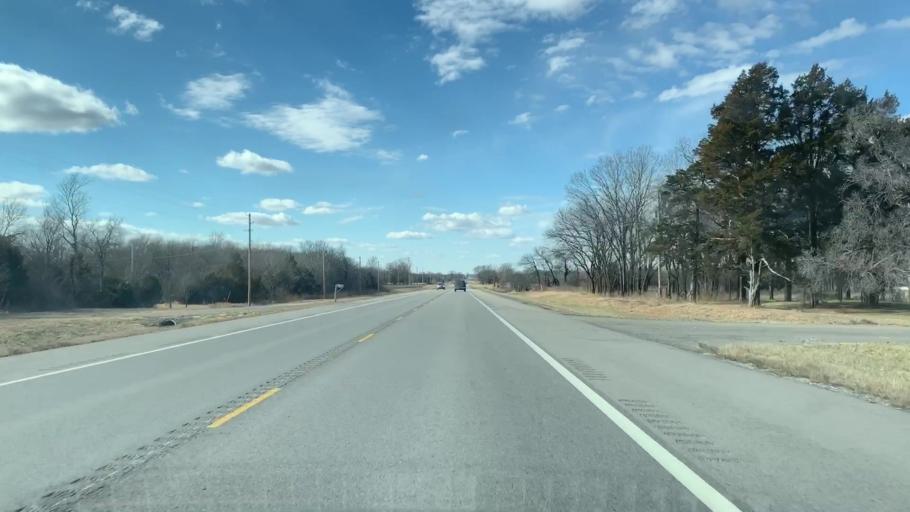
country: US
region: Kansas
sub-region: Labette County
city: Oswego
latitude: 37.3401
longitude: -95.0605
